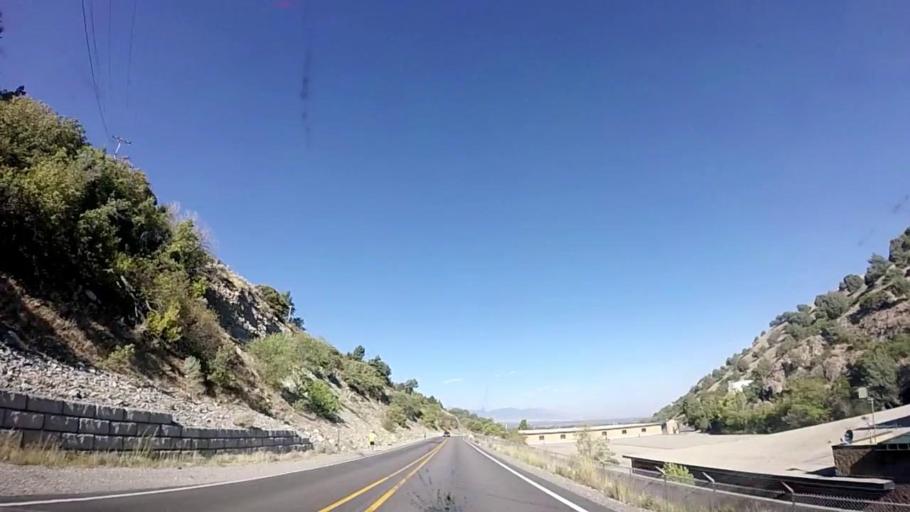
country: US
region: Utah
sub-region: Salt Lake County
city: Cottonwood Heights
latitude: 40.6186
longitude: -111.7821
